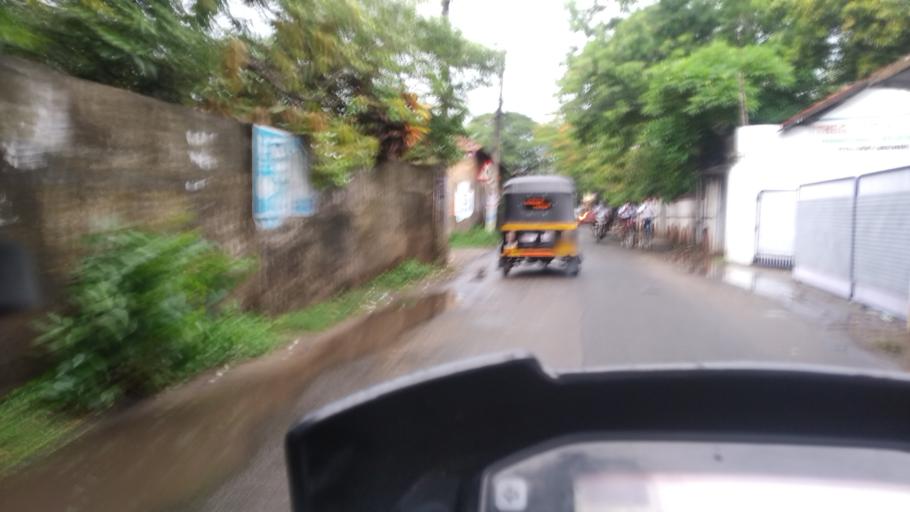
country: IN
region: Kerala
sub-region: Alappuzha
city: Alleppey
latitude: 9.5011
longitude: 76.3214
